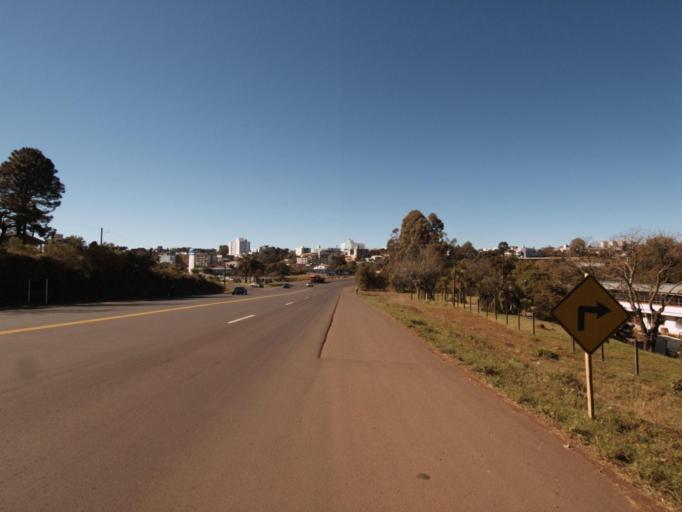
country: BR
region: Santa Catarina
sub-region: Xanxere
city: Xanxere
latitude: -26.8833
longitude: -52.4066
